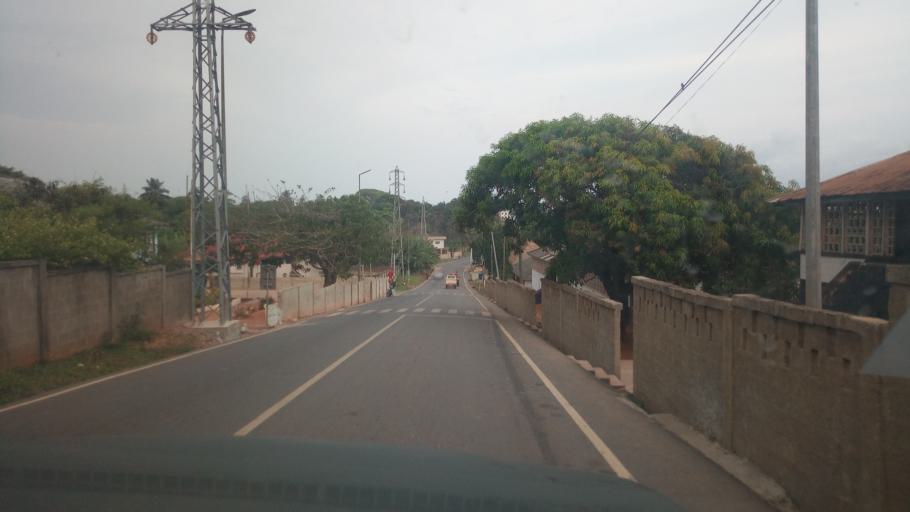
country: GH
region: Western
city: Takoradi
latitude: 4.8797
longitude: -1.7609
